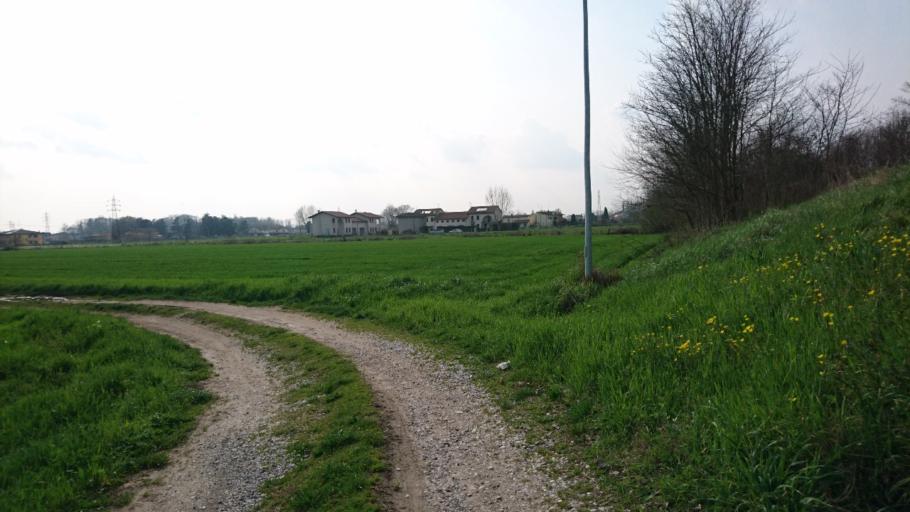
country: IT
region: Veneto
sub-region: Provincia di Padova
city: San Vito
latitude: 45.4184
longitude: 11.9785
